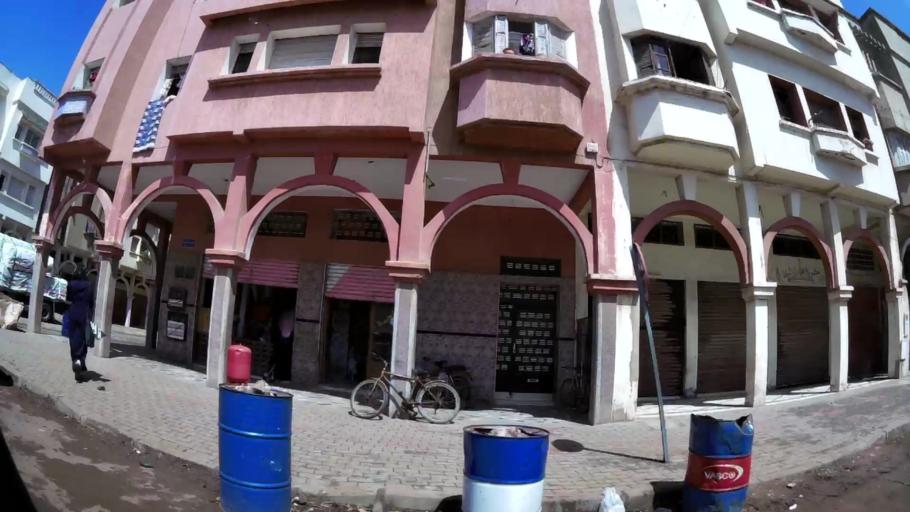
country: MA
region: Grand Casablanca
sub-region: Mohammedia
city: Mohammedia
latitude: 33.6380
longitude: -7.4524
